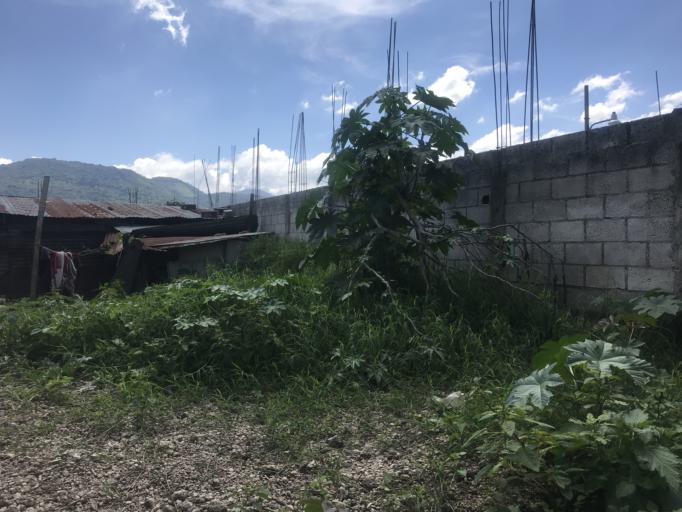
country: GT
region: Guatemala
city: Amatitlan
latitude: 14.4792
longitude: -90.6328
